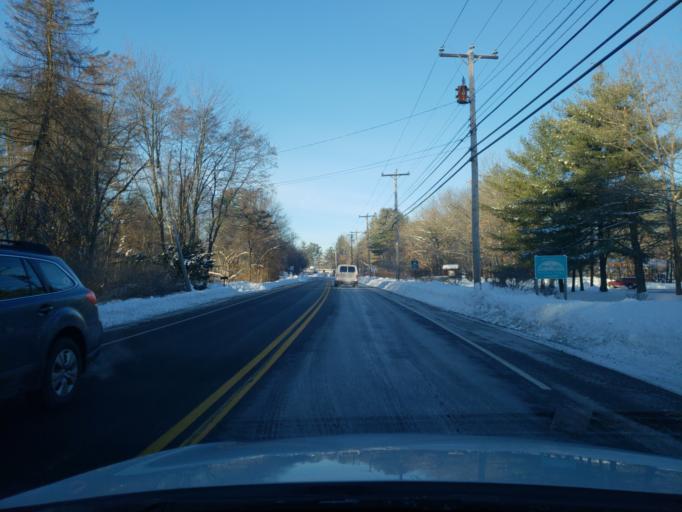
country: US
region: New Hampshire
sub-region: Hillsborough County
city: Goffstown
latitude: 43.0146
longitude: -71.5799
